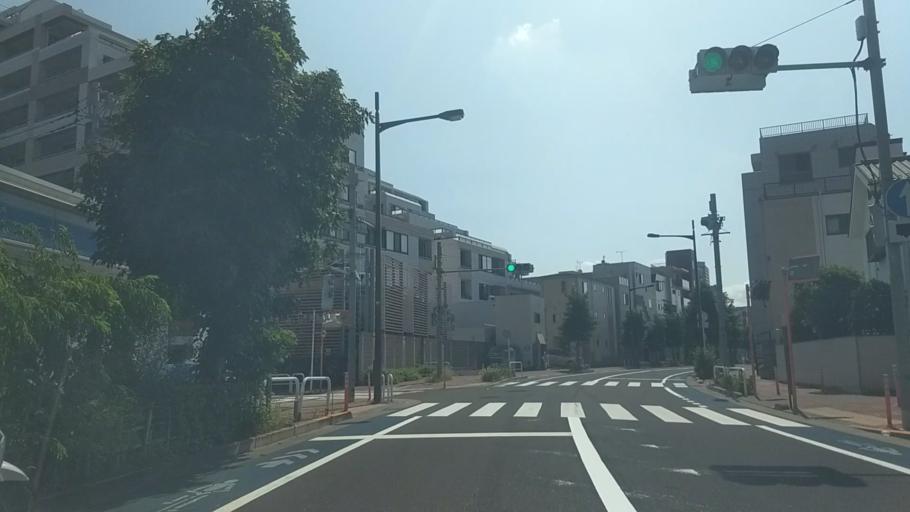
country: JP
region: Kanagawa
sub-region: Kawasaki-shi
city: Kawasaki
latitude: 35.6035
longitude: 139.7292
